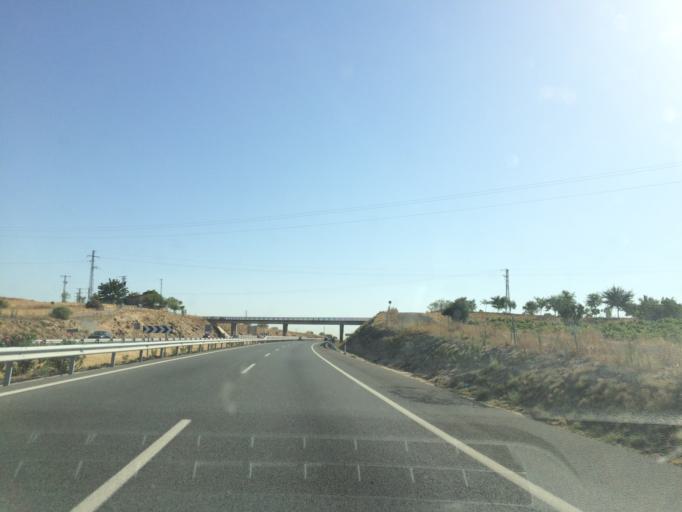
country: ES
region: Castille-La Mancha
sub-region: Province of Toledo
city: Valmojado
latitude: 40.2121
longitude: -4.0974
